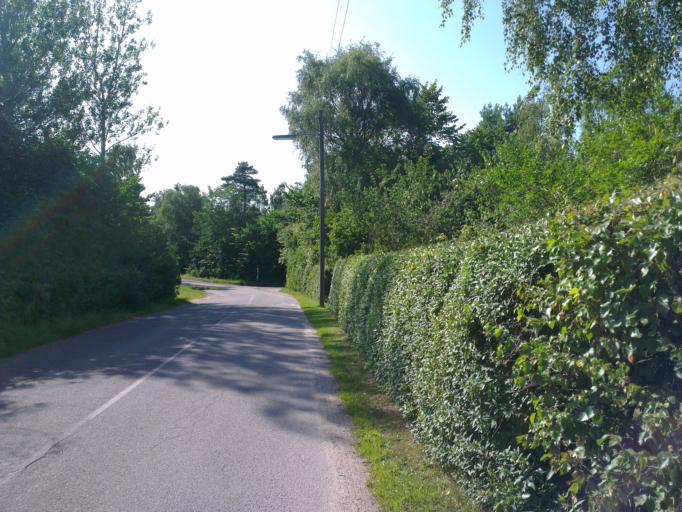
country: DK
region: Capital Region
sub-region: Halsnaes Kommune
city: Liseleje
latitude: 55.9290
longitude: 11.9365
